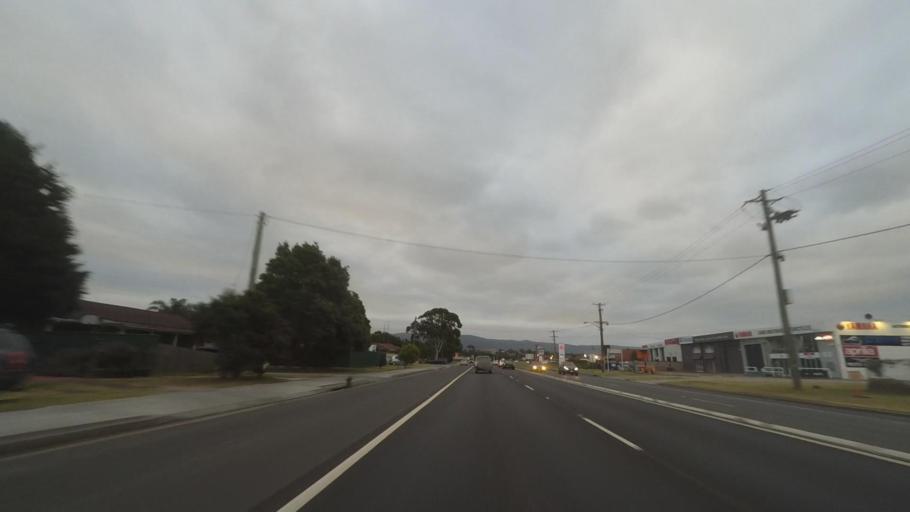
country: AU
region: New South Wales
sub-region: Shellharbour
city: Albion Park Rail
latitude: -34.5519
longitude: 150.7877
